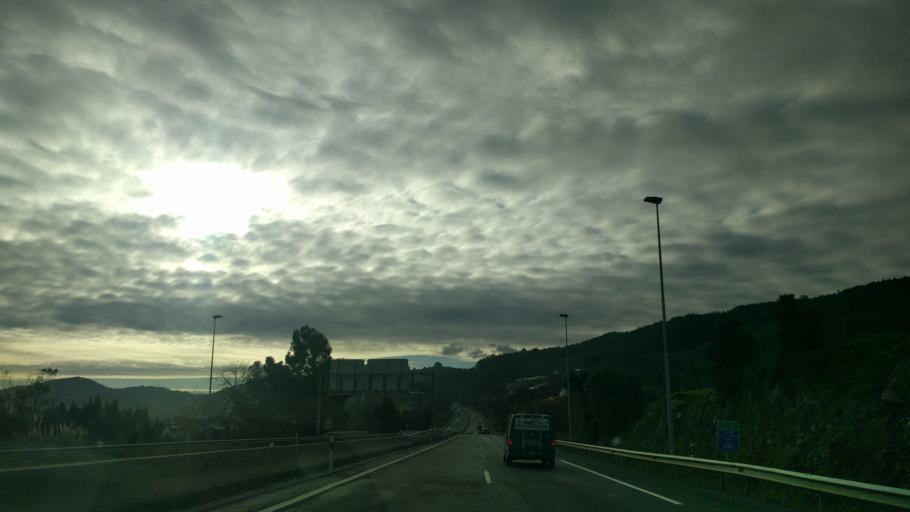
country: ES
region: Cantabria
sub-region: Provincia de Cantabria
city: Castro-Urdiales
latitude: 43.3909
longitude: -3.2345
